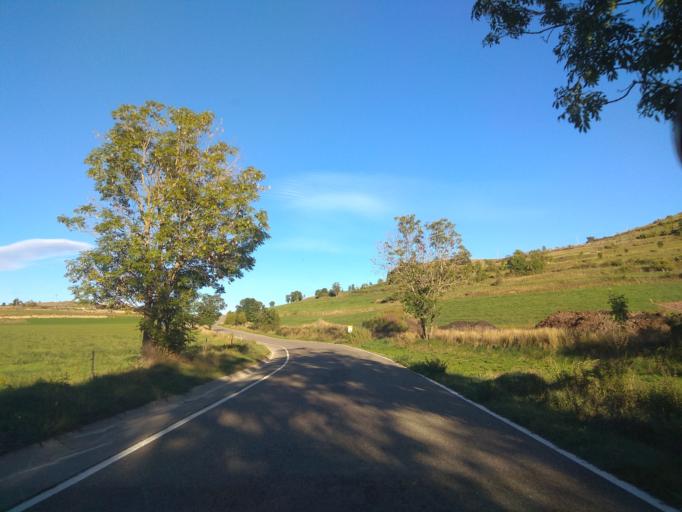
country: ES
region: Catalonia
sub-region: Provincia de Lleida
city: Lles de Cerdanya
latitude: 42.3507
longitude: 1.6943
